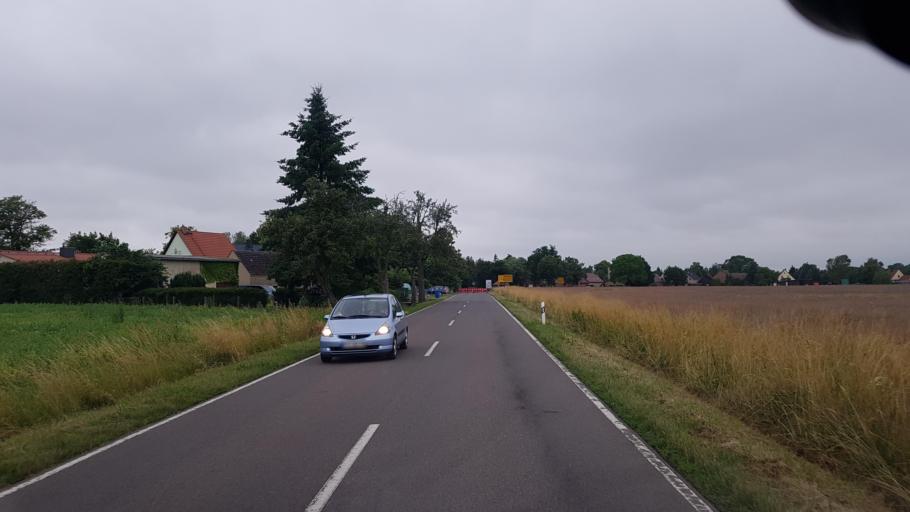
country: DE
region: Brandenburg
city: Juterbog
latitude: 51.9330
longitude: 13.2000
